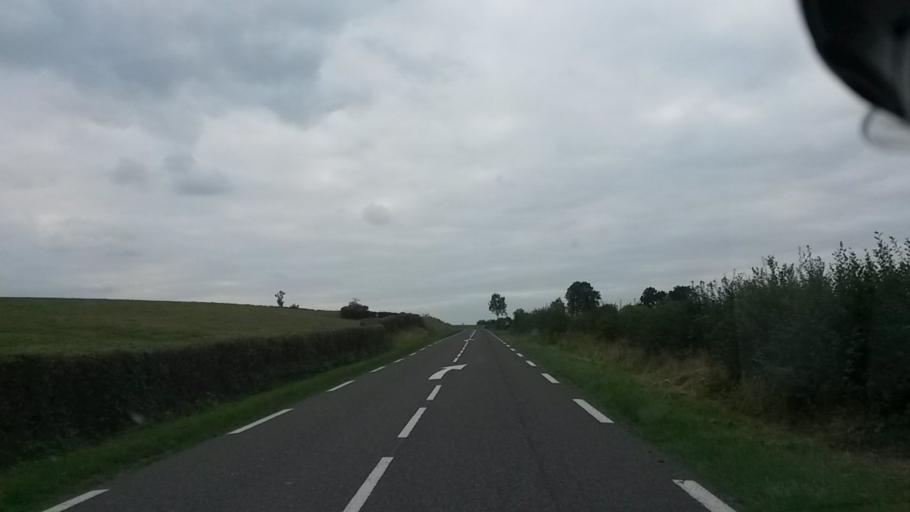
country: FR
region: Haute-Normandie
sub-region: Departement de la Seine-Maritime
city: Forges-les-Eaux
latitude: 49.5633
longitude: 1.5214
